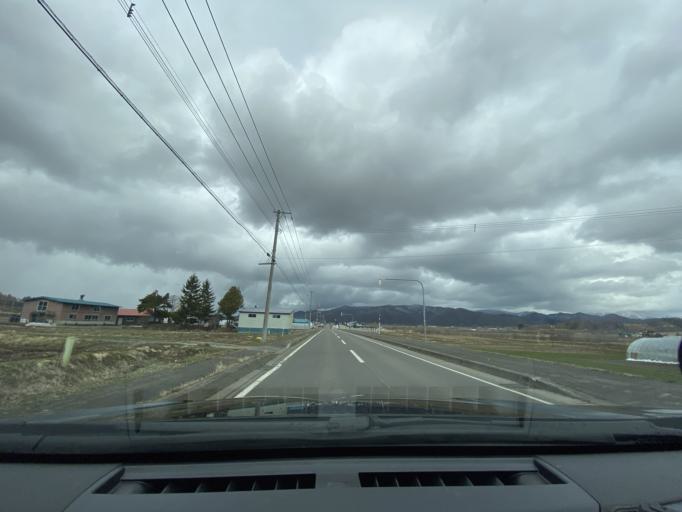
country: JP
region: Hokkaido
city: Nayoro
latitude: 44.1073
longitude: 142.4778
